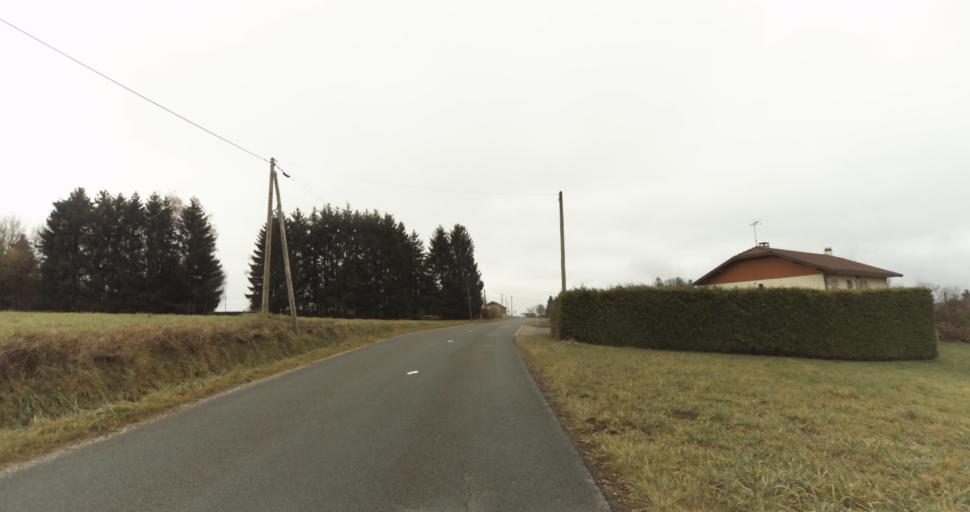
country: FR
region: Rhone-Alpes
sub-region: Departement de la Haute-Savoie
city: Groisy
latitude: 46.0386
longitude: 6.1871
